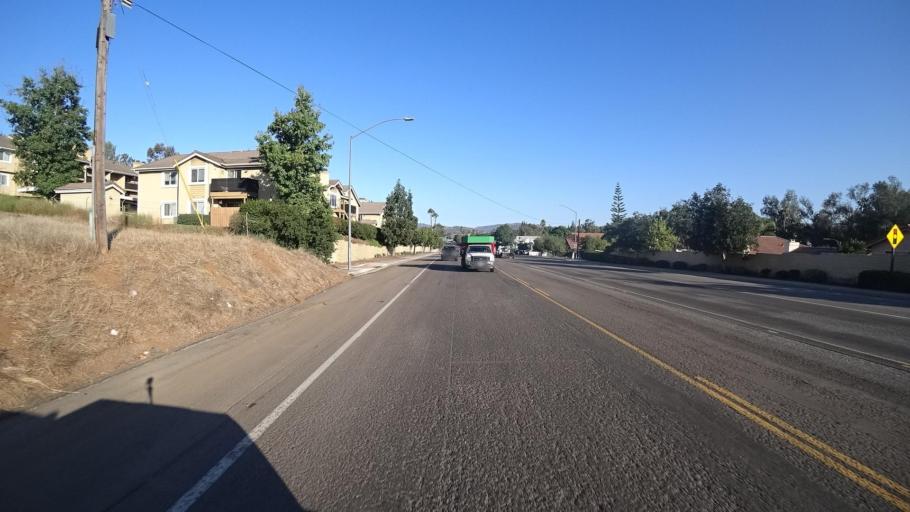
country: US
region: California
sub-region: San Diego County
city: Escondido
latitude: 33.1230
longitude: -117.0621
